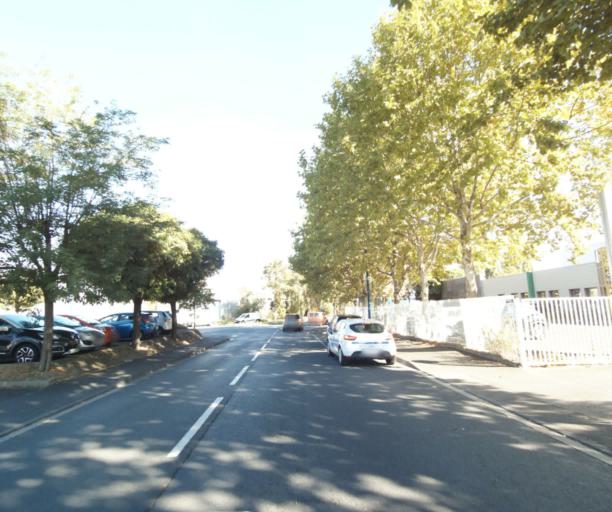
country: FR
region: Auvergne
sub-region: Departement du Puy-de-Dome
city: Aubiere
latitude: 45.7805
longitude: 3.1213
